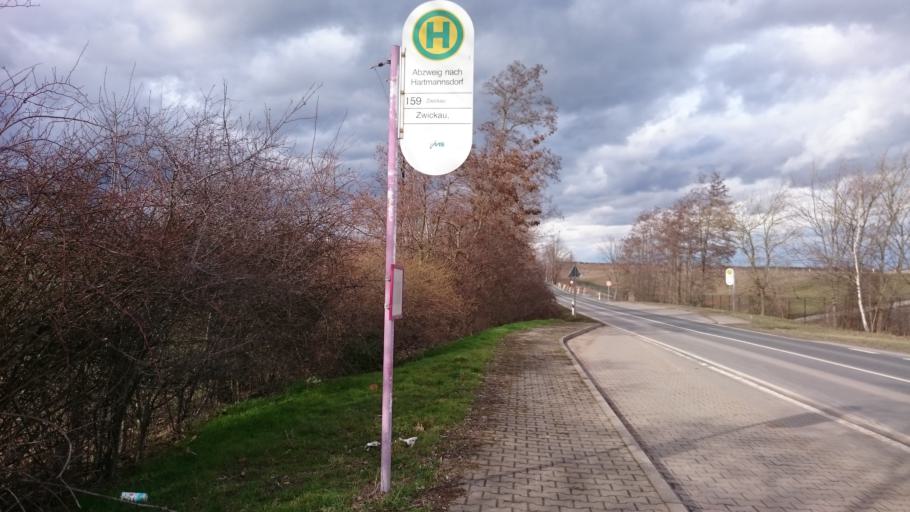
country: DE
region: Saxony
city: Hartmannsdorf
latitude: 50.7566
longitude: 12.4367
